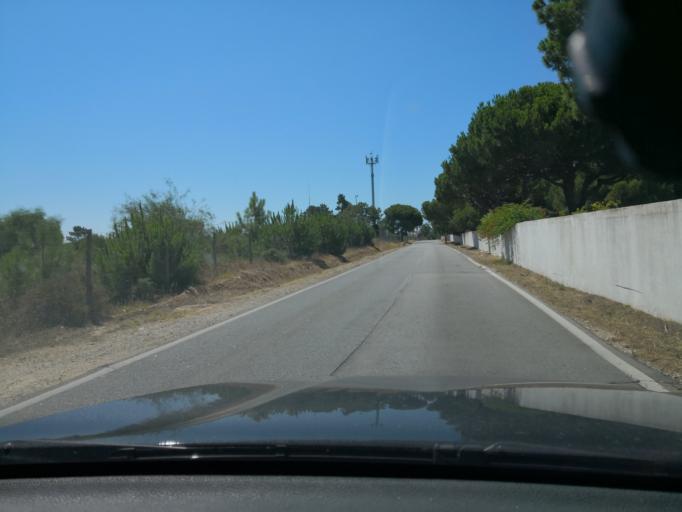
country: PT
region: Faro
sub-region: Loule
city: Vilamoura
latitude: 37.0826
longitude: -8.1000
